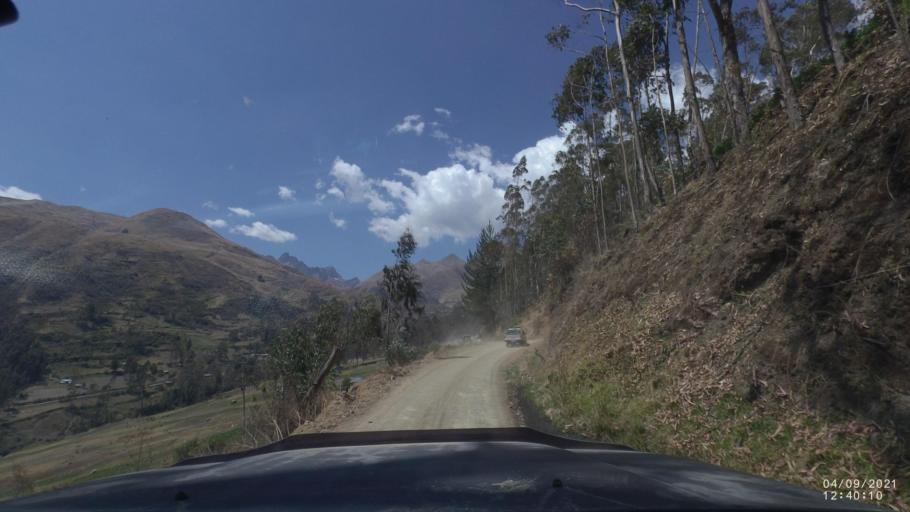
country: BO
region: Cochabamba
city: Colchani
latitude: -17.2294
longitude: -66.4975
